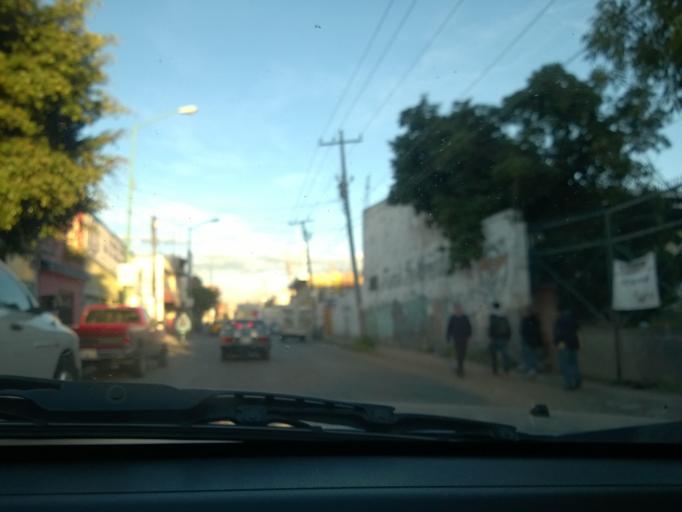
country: MX
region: Guanajuato
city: Leon
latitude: 21.1238
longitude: -101.6606
